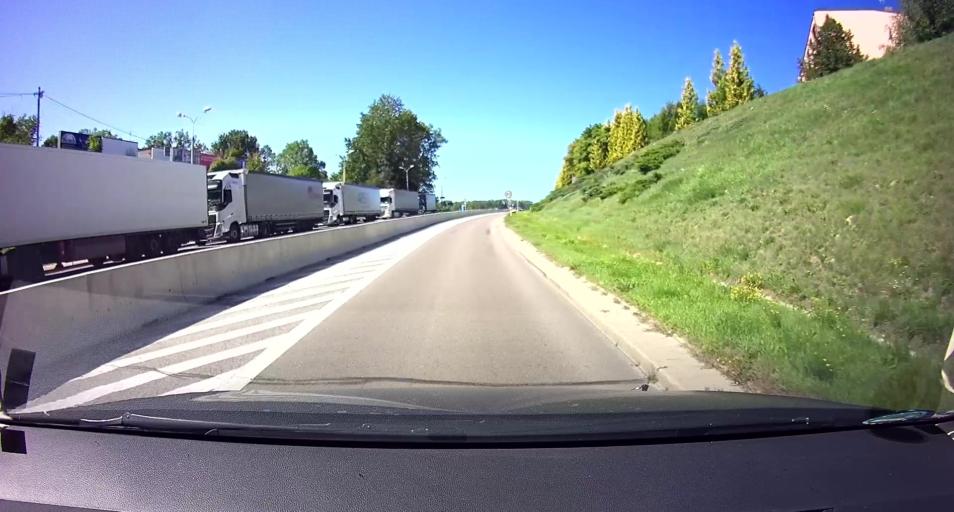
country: BY
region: Grodnenskaya
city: Vyalikaya Byerastavitsa
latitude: 53.1240
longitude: 23.8850
